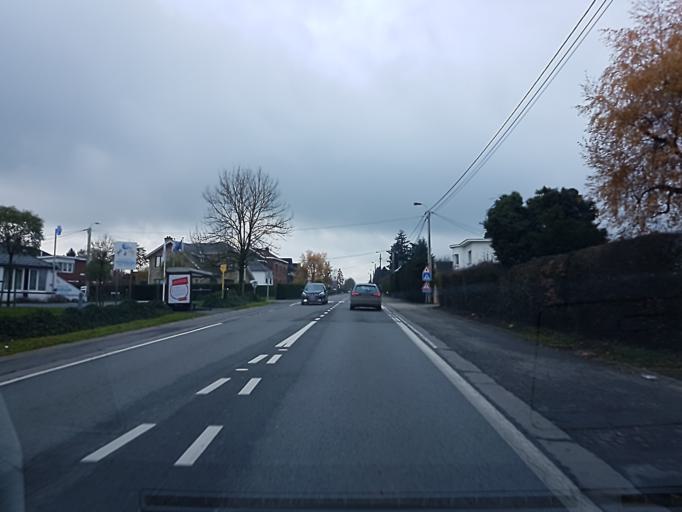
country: BE
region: Wallonia
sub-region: Province de Liege
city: Verviers
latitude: 50.5664
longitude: 5.8675
